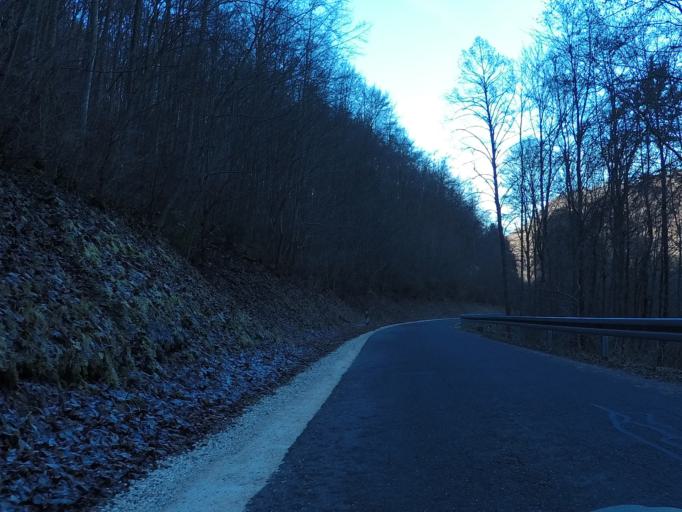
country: DE
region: Baden-Wuerttemberg
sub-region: Tuebingen Region
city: Sankt Johann
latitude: 48.4433
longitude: 9.2945
